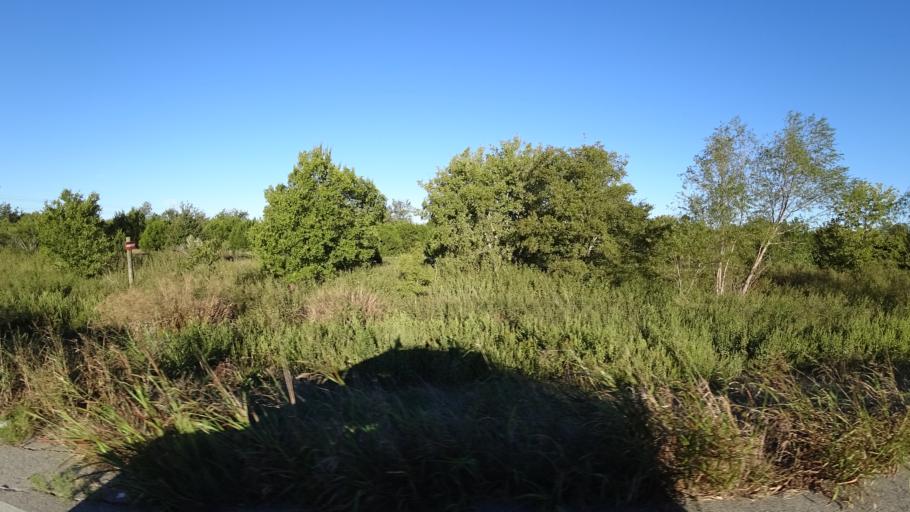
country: US
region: Texas
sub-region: Travis County
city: Manor
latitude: 30.3163
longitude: -97.6343
